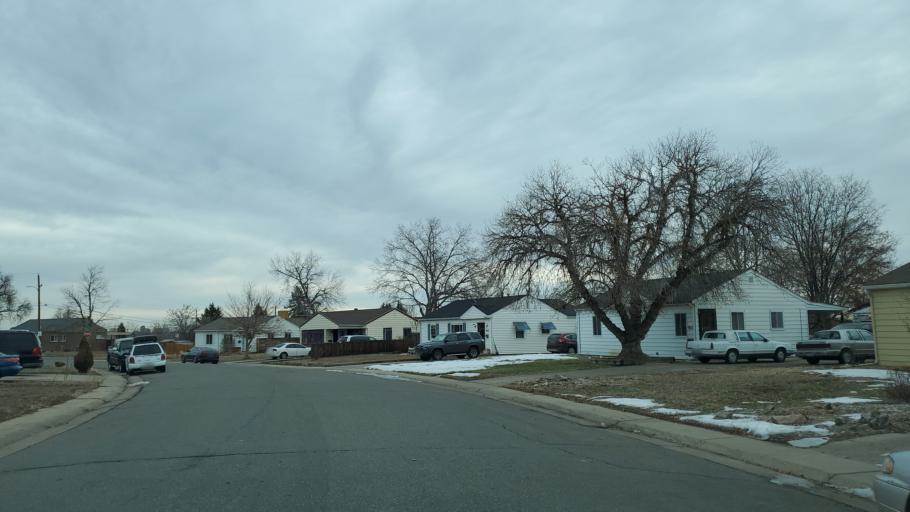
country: US
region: Colorado
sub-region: Denver County
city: Denver
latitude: 39.6983
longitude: -105.0050
